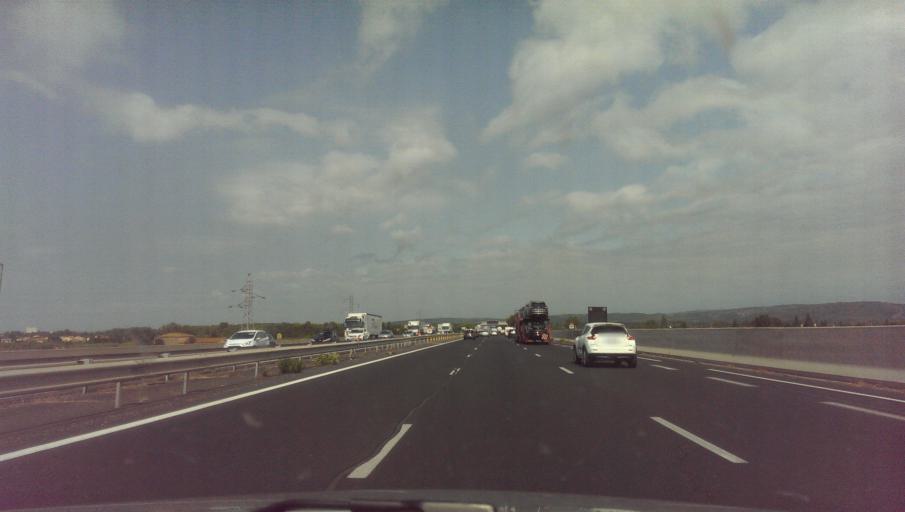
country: FR
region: Languedoc-Roussillon
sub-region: Departement de l'Aude
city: Narbonne
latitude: 43.1676
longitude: 3.0043
